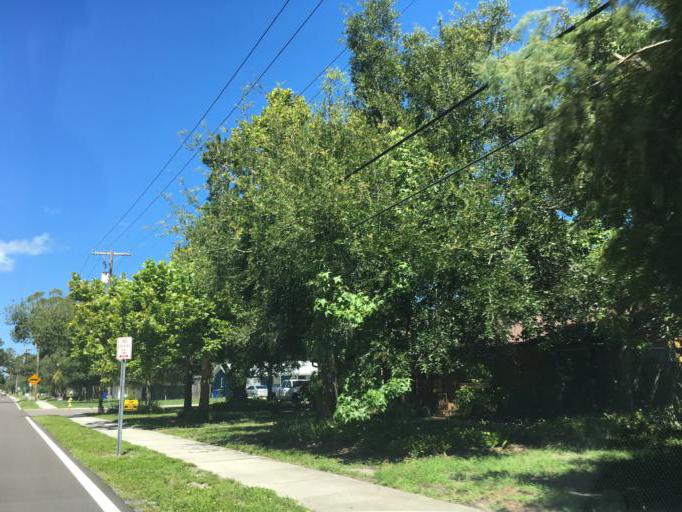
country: US
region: Florida
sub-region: Pinellas County
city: Dunedin
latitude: 28.0378
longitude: -82.7758
